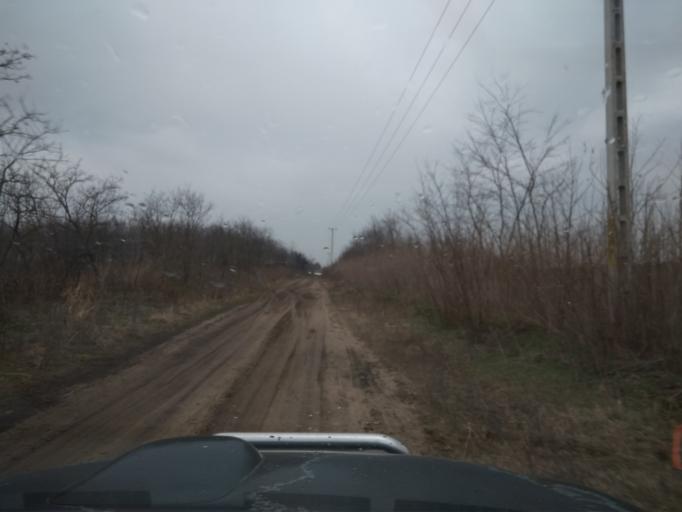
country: HU
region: Szabolcs-Szatmar-Bereg
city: Nyirpazony
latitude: 48.0042
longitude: 21.7888
